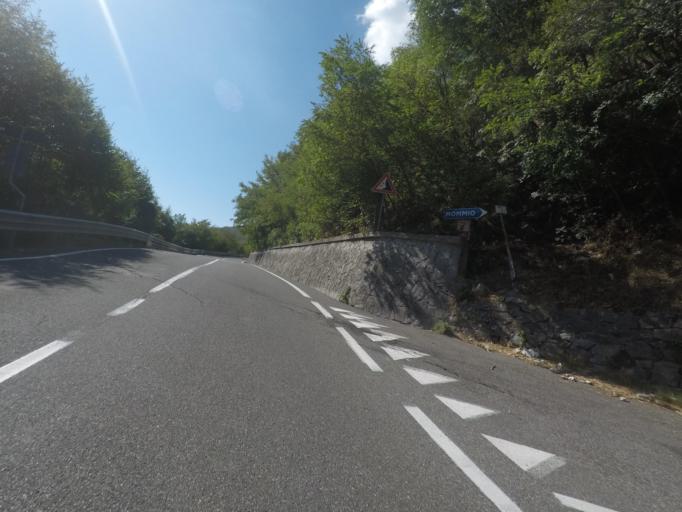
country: IT
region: Tuscany
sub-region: Provincia di Massa-Carrara
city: Casola in Lunigiana
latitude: 44.2514
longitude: 10.1767
